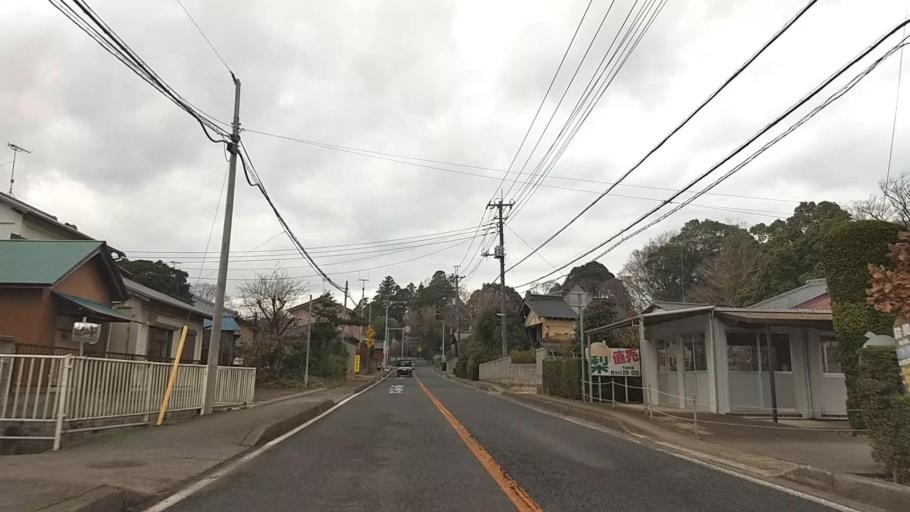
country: JP
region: Chiba
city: Yotsukaido
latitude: 35.5815
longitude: 140.2349
